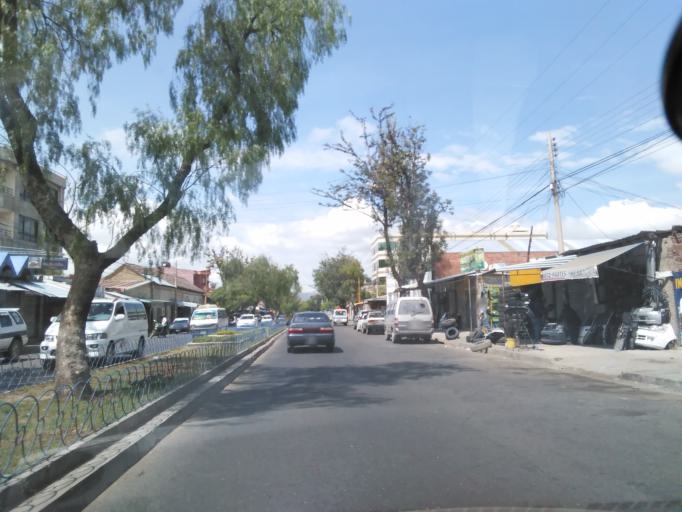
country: BO
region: Cochabamba
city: Cochabamba
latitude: -17.4052
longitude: -66.1636
